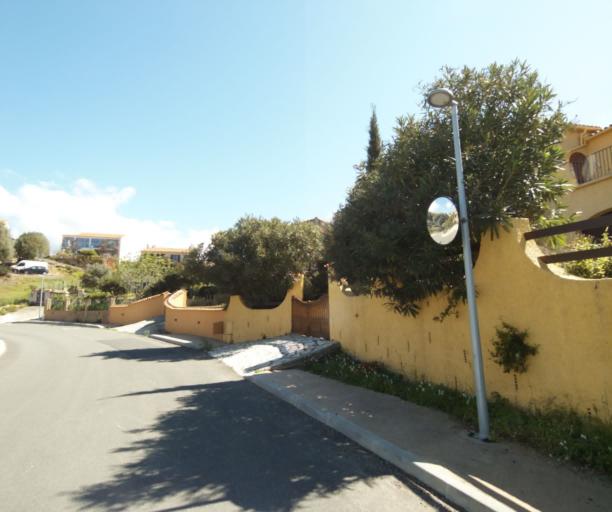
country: FR
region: Corsica
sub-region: Departement de la Corse-du-Sud
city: Propriano
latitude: 41.6750
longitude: 8.9110
